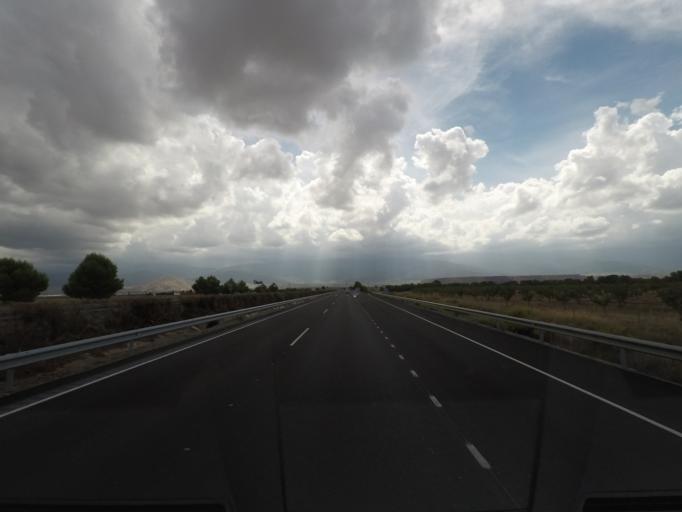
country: ES
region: Andalusia
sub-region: Provincia de Granada
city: Albunan
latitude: 37.2340
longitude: -3.0823
